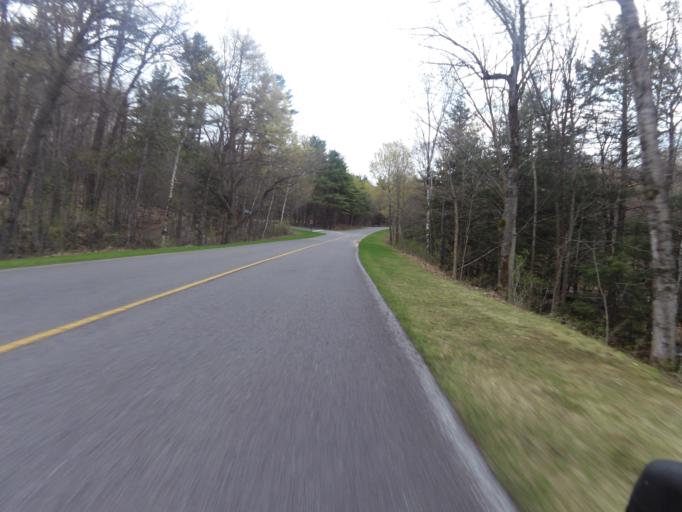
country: CA
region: Quebec
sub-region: Outaouais
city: Gatineau
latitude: 45.4806
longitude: -75.8493
